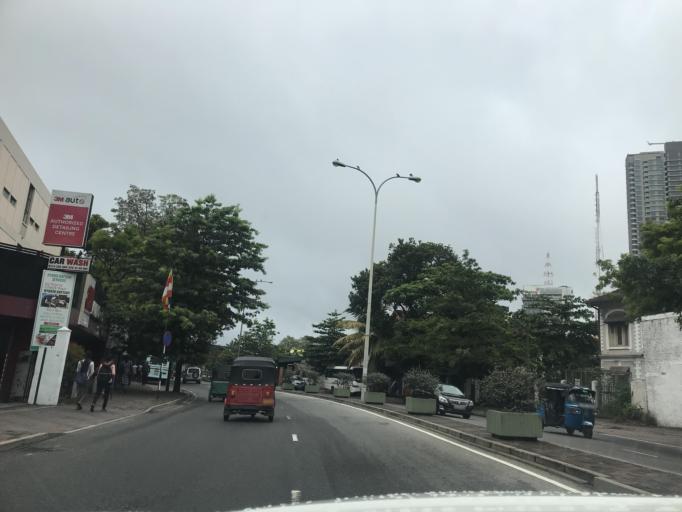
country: LK
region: Western
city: Colombo
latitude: 6.9215
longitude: 79.8644
